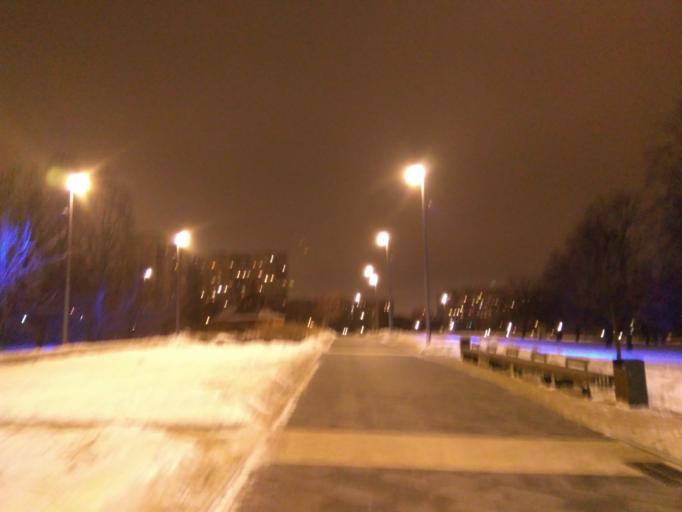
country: RU
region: Moscow
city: Tsaritsyno
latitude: 55.6591
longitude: 37.6500
